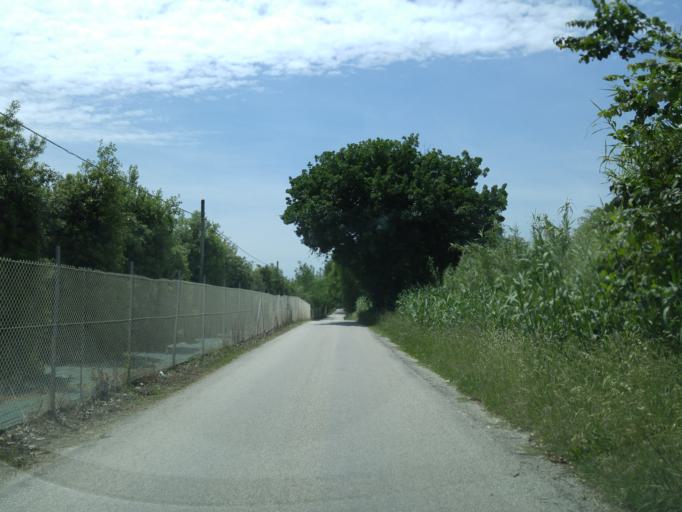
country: IT
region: The Marches
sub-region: Provincia di Pesaro e Urbino
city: Bellocchi
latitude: 43.7849
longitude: 13.0096
